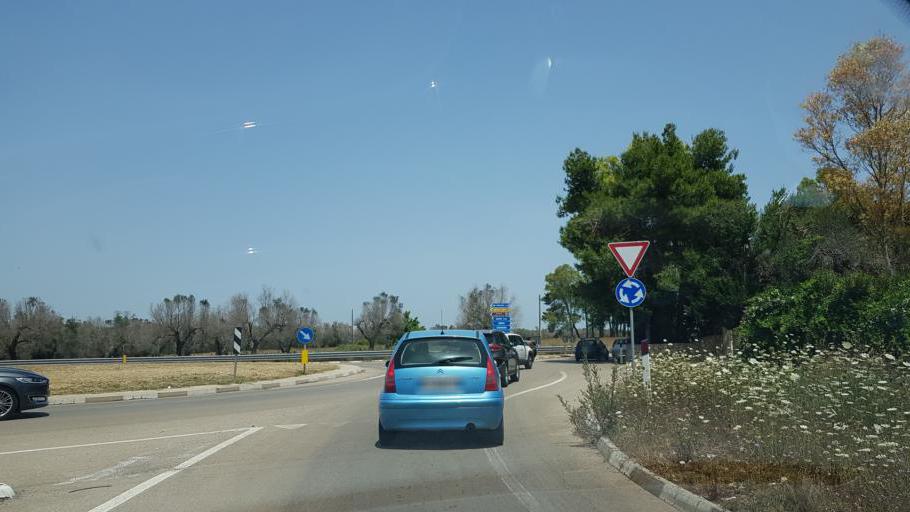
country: IT
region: Apulia
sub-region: Provincia di Lecce
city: Veglie
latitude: 40.3261
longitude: 17.9255
